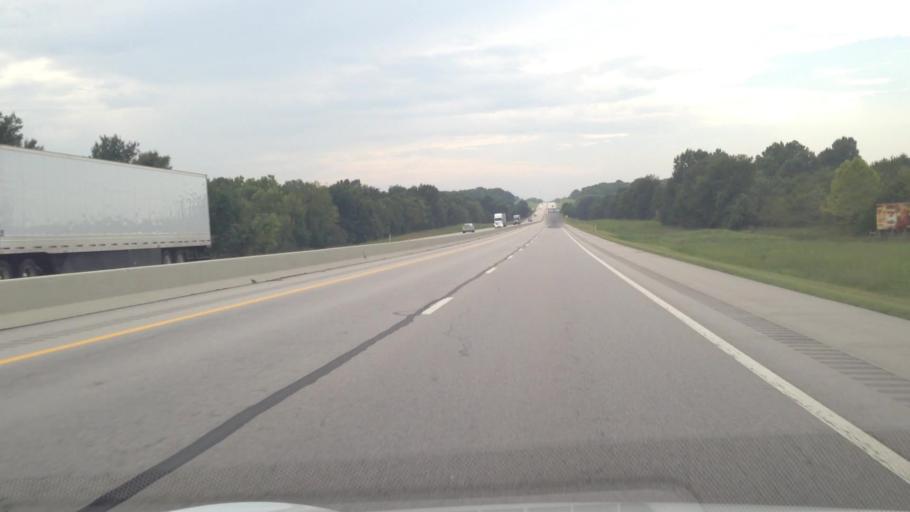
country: US
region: Kansas
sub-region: Cherokee County
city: Baxter Springs
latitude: 36.9289
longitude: -94.7312
